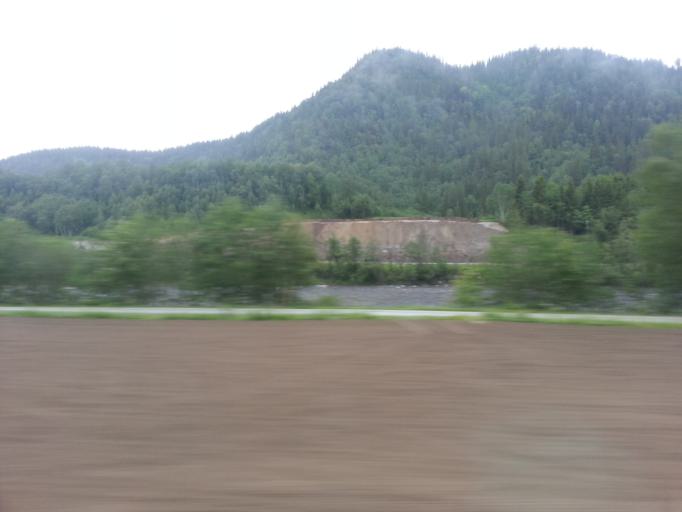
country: NO
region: Sor-Trondelag
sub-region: Midtre Gauldal
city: Storen
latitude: 63.0683
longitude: 10.2741
